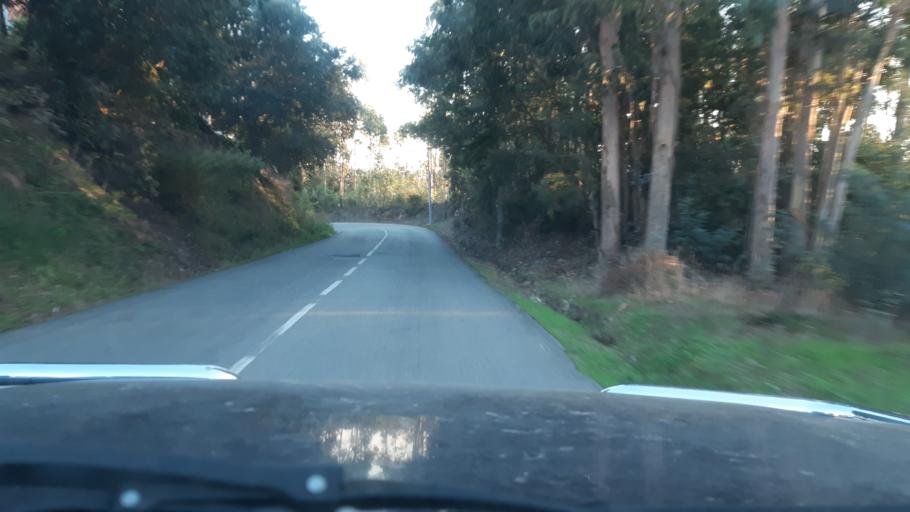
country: PT
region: Aveiro
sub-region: Agueda
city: Agueda
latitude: 40.5791
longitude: -8.4633
